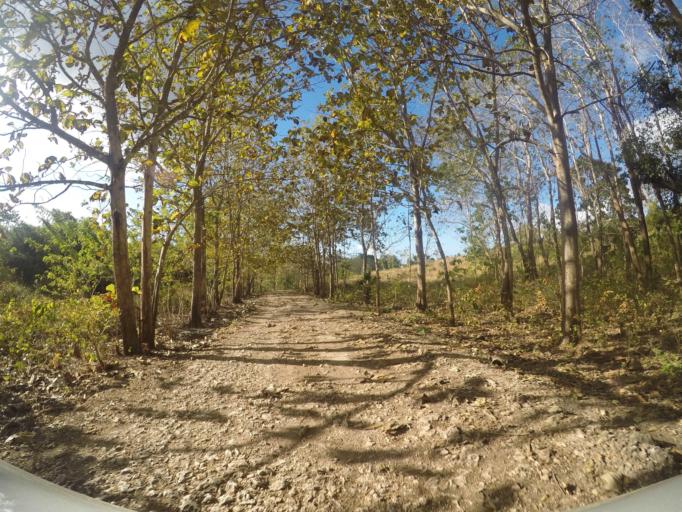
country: TL
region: Lautem
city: Lospalos
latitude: -8.4620
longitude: 126.8859
